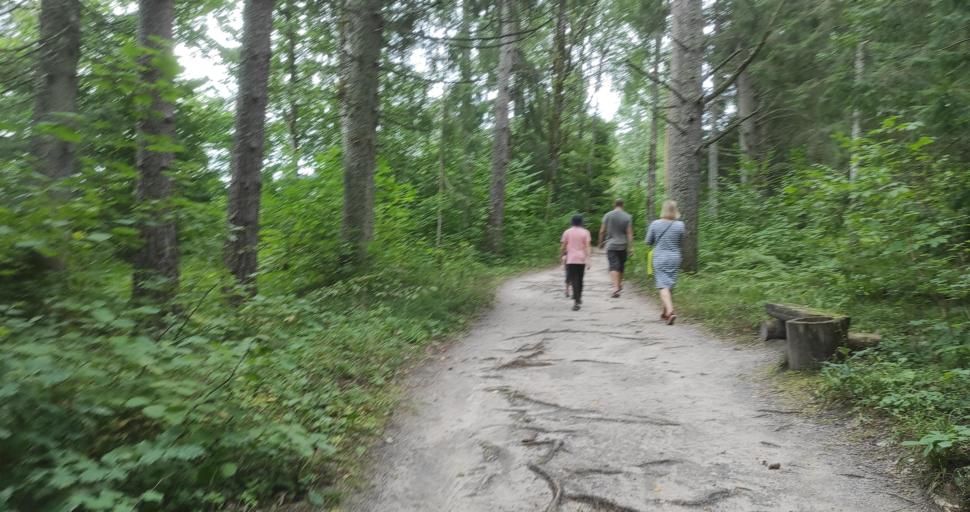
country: LV
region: Kuldigas Rajons
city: Kuldiga
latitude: 57.0071
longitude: 21.9847
